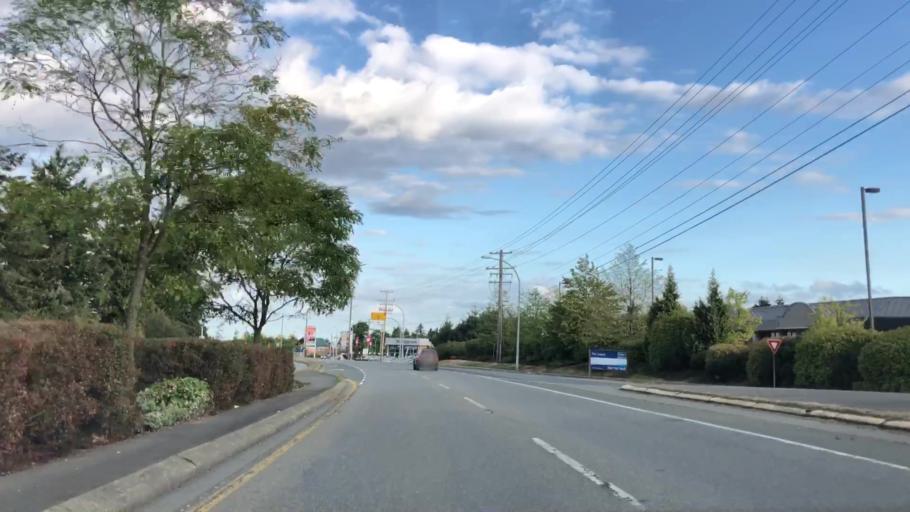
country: CA
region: British Columbia
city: Nanaimo
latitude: 49.2371
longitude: -124.0466
